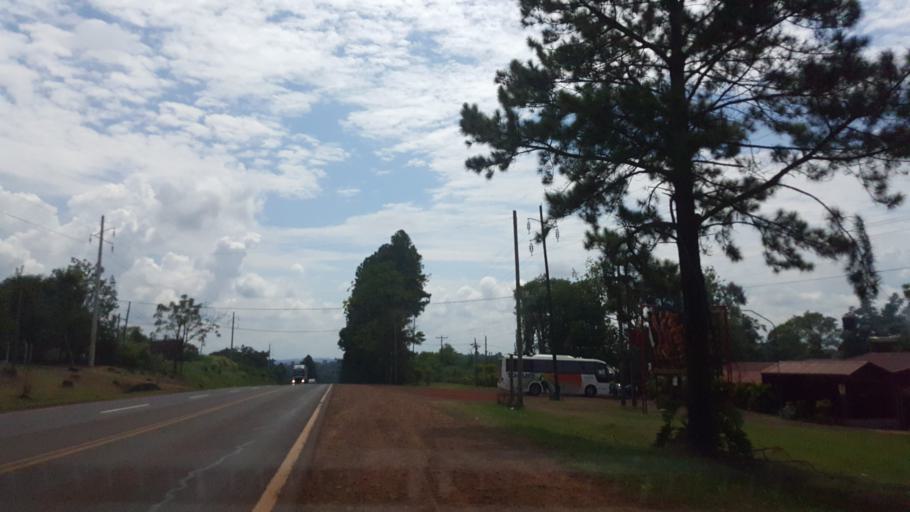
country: AR
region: Misiones
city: Puerto Rico
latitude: -26.8389
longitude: -55.0389
